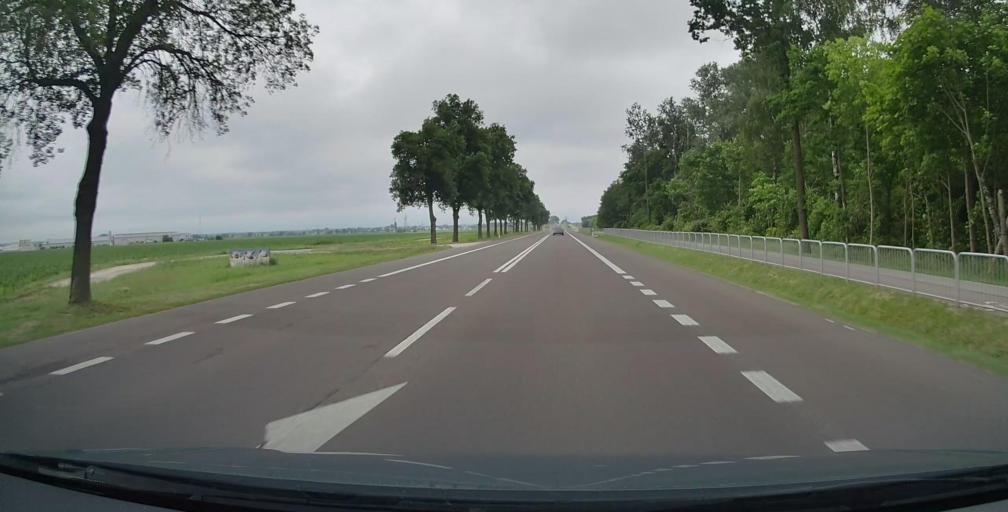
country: PL
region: Lublin Voivodeship
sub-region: Powiat bialski
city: Miedzyrzec Podlaski
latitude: 52.0094
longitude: 22.7426
